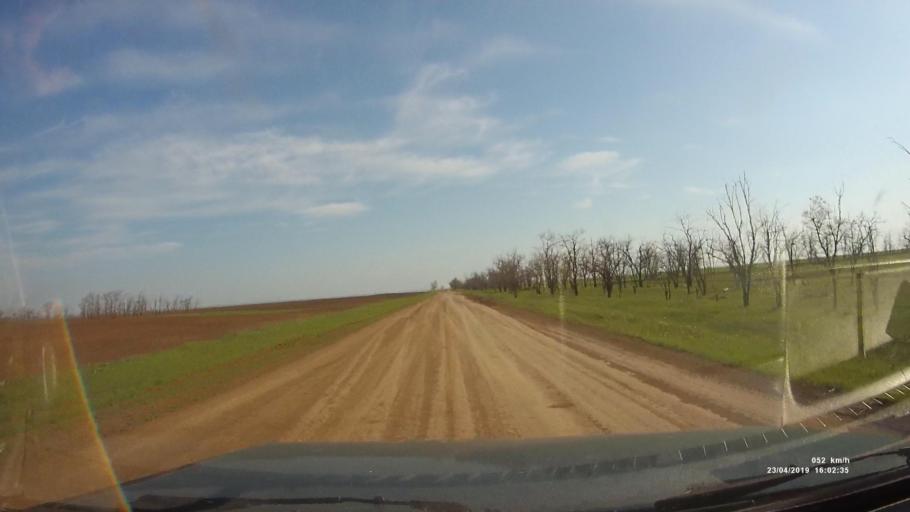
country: RU
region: Rostov
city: Remontnoye
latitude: 46.4927
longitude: 43.1072
